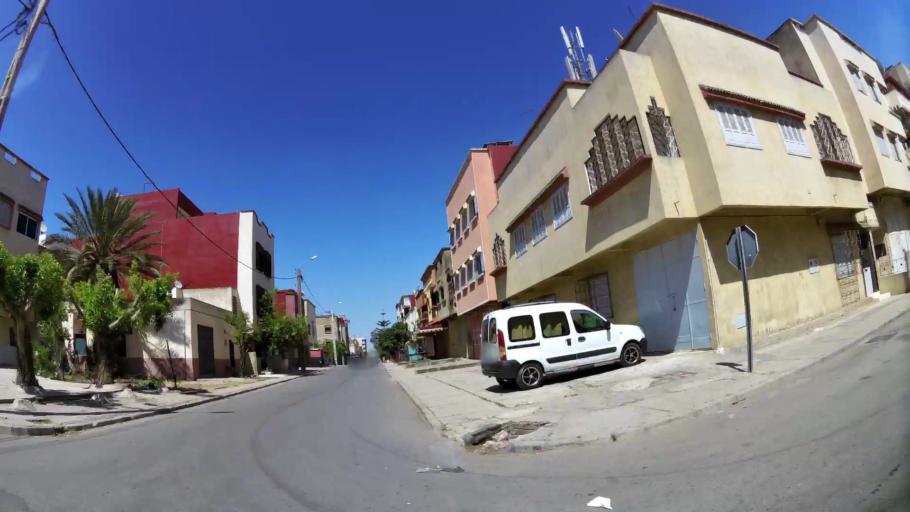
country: MA
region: Gharb-Chrarda-Beni Hssen
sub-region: Kenitra Province
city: Kenitra
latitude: 34.2405
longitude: -6.5523
